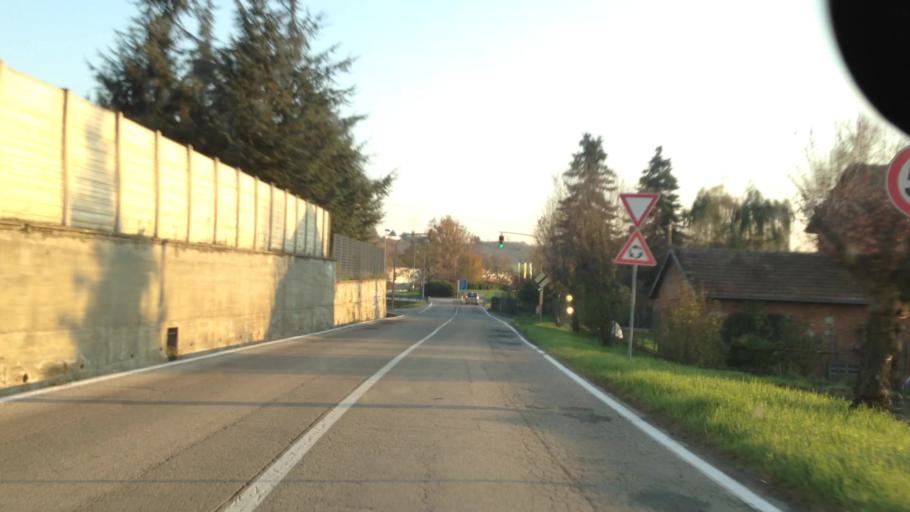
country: IT
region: Piedmont
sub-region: Provincia di Asti
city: Montiglio
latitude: 45.0665
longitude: 8.1116
